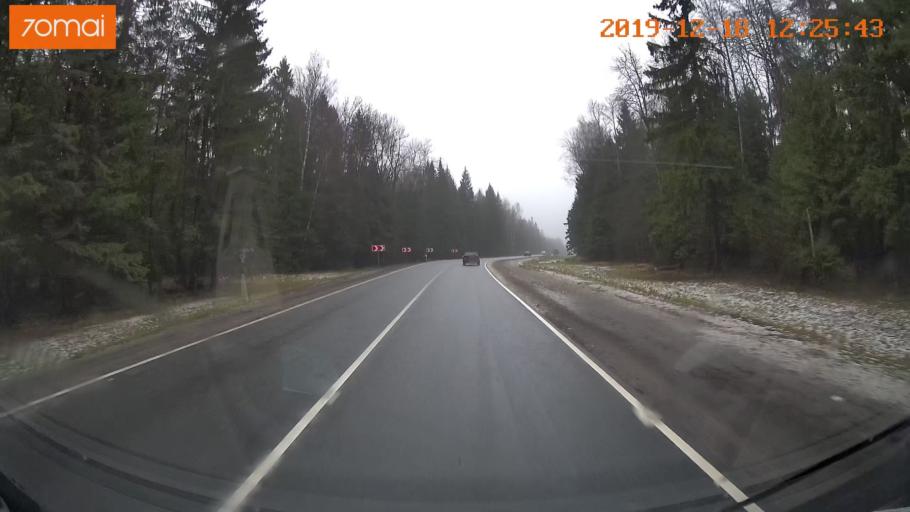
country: RU
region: Moskovskaya
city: Novopetrovskoye
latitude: 56.0420
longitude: 36.4989
